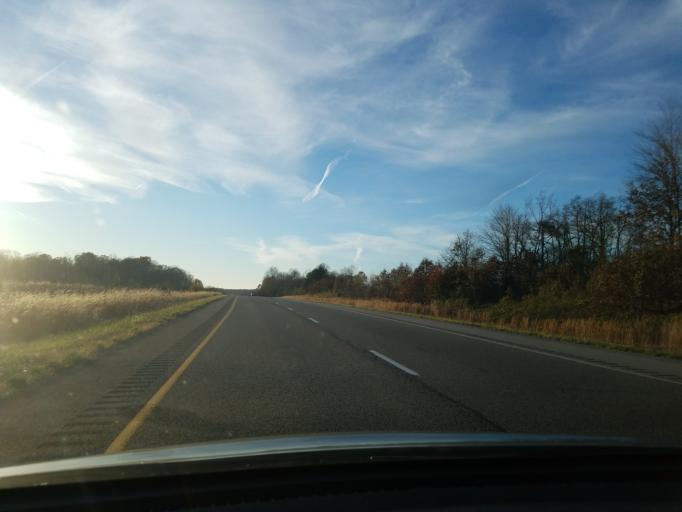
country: US
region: Indiana
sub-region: Spencer County
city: Dale
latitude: 38.1989
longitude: -87.1542
